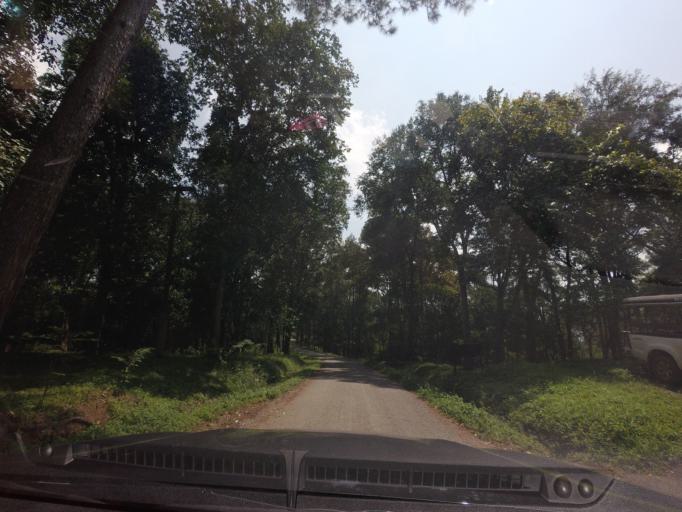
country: TH
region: Loei
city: Phu Ruea
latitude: 17.4812
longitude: 101.3520
